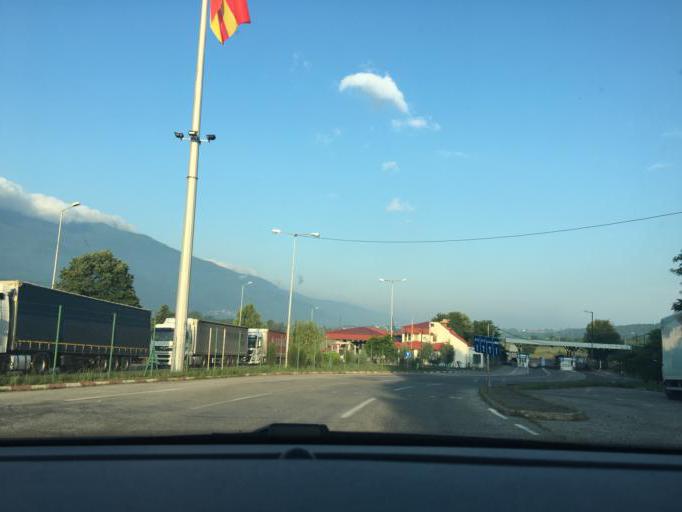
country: MK
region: Novo Selo
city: Novo Selo
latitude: 41.3965
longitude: 22.9654
